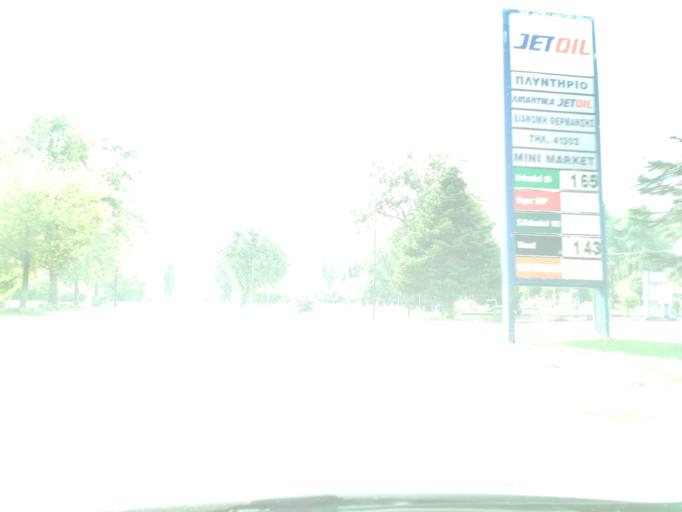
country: GR
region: Central Greece
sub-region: Nomos Evvoias
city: Prokopion
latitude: 38.7235
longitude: 23.5077
